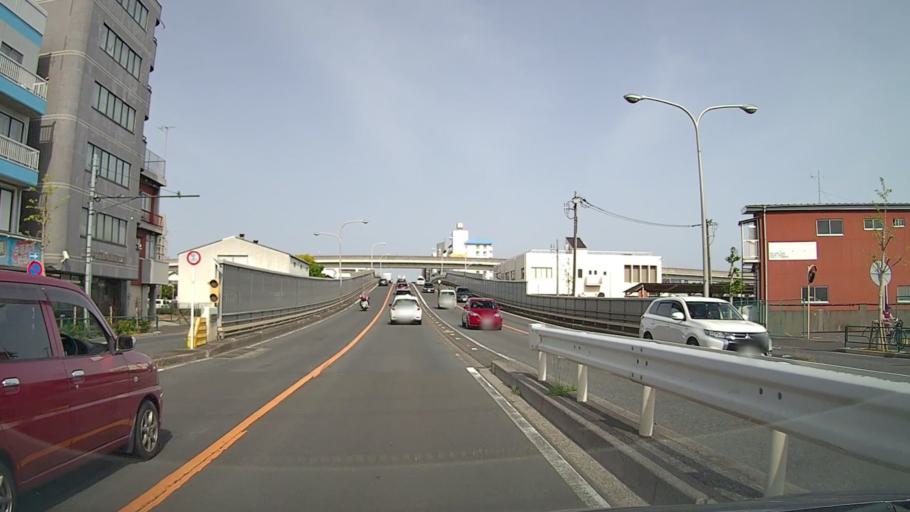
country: JP
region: Saitama
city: Soka
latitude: 35.7783
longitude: 139.7682
